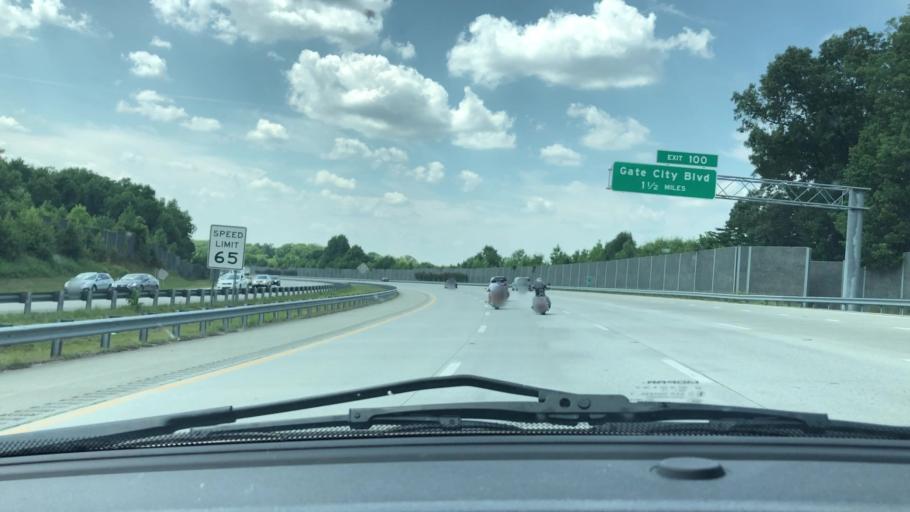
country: US
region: North Carolina
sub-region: Guilford County
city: Greensboro
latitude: 36.0180
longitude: -79.8532
